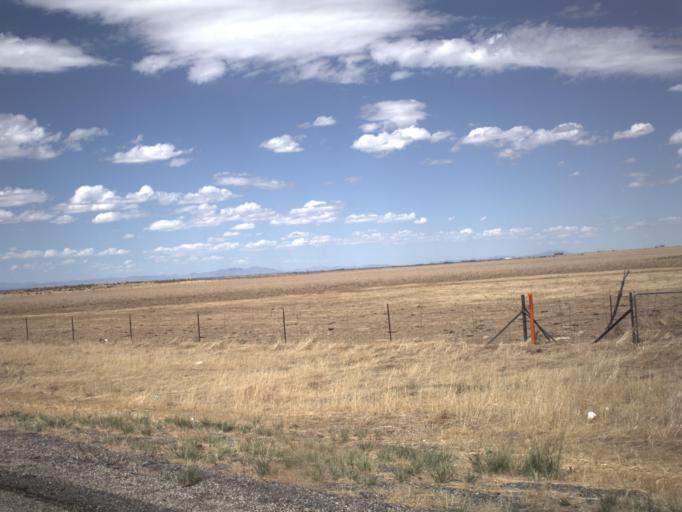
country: US
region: Utah
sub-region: Millard County
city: Fillmore
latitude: 39.1144
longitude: -112.2945
